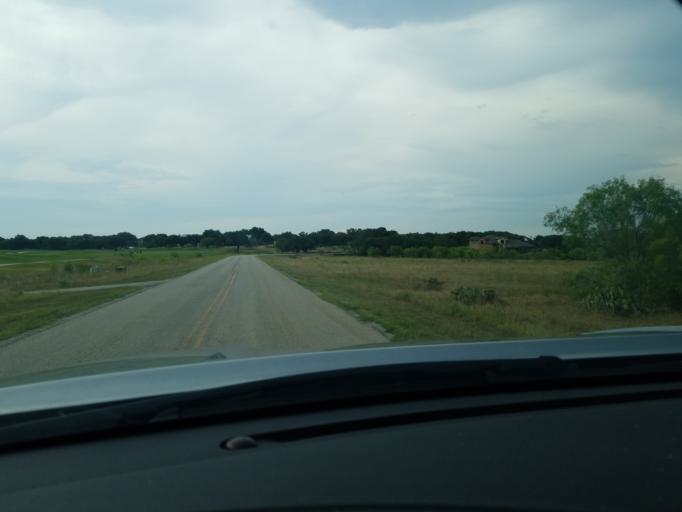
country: US
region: Texas
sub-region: Comal County
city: Bulverde
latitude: 29.8447
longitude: -98.4041
